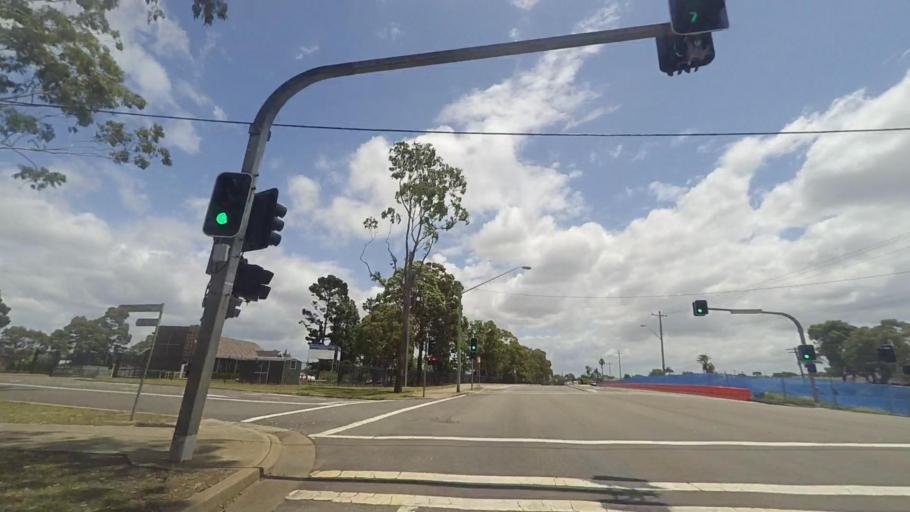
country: AU
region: New South Wales
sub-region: Bankstown
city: Milperra
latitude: -33.9532
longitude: 150.9531
